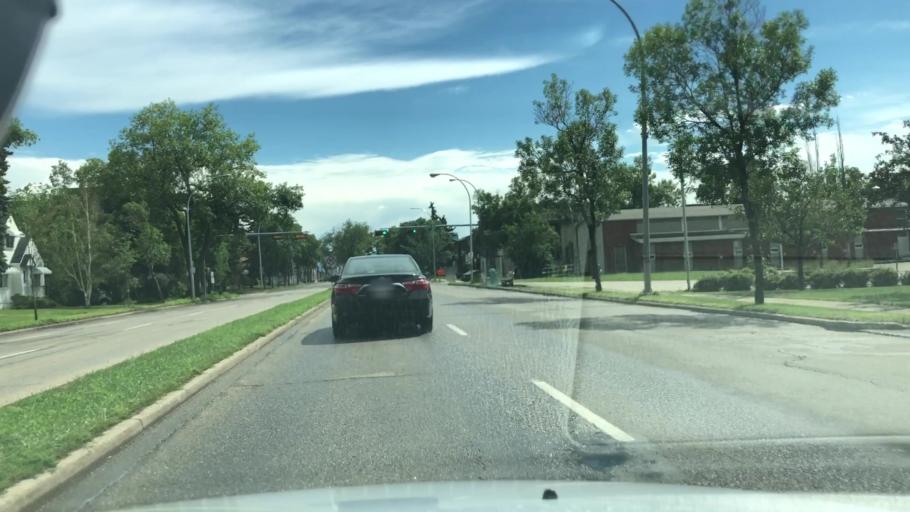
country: CA
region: Alberta
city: Edmonton
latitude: 53.5539
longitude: -113.5086
